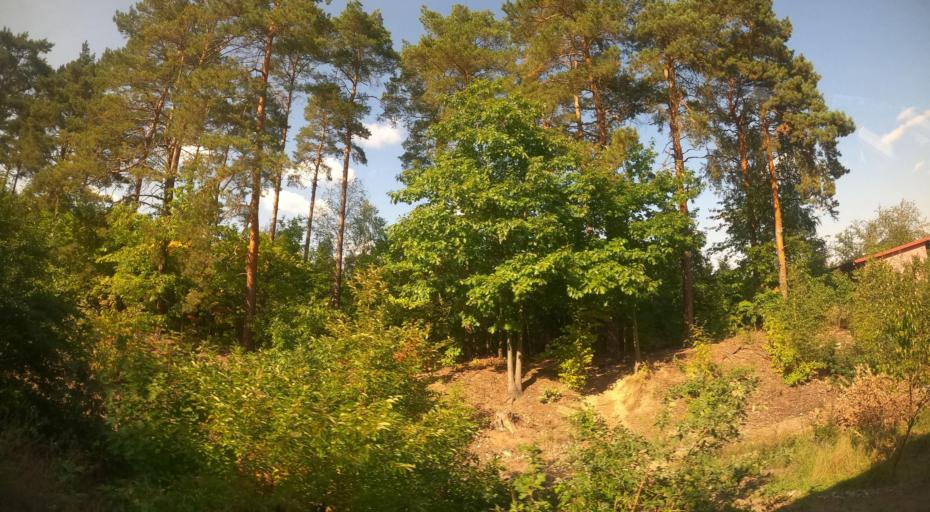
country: PL
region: Lubusz
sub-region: Zielona Gora
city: Zielona Gora
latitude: 51.9469
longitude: 15.4702
